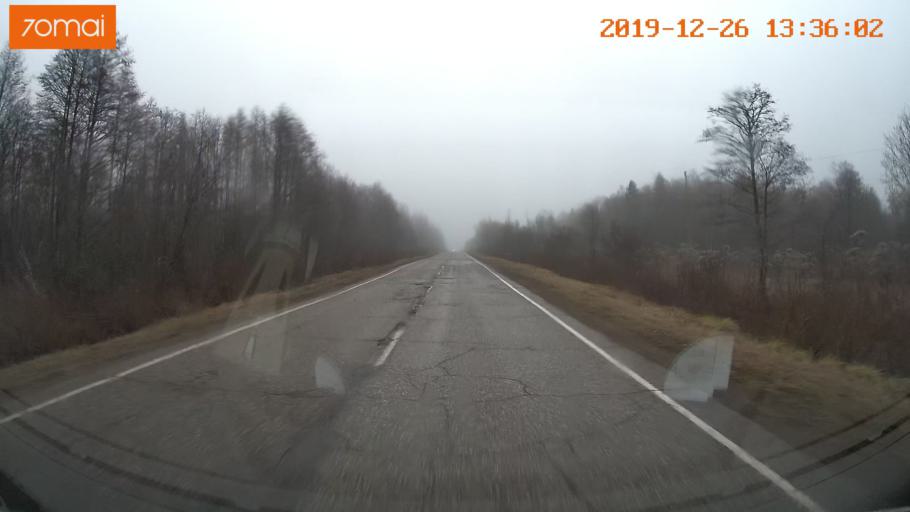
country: RU
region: Vologda
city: Sheksna
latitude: 58.7870
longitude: 38.3489
